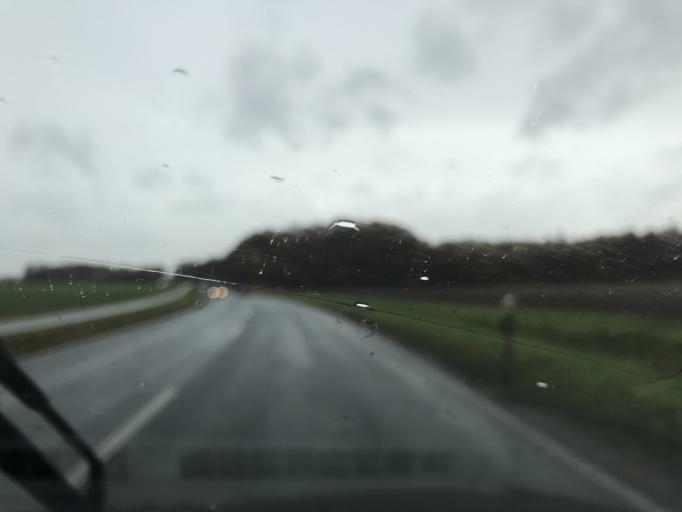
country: DE
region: North Rhine-Westphalia
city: Oelde
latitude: 51.8454
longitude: 8.1829
